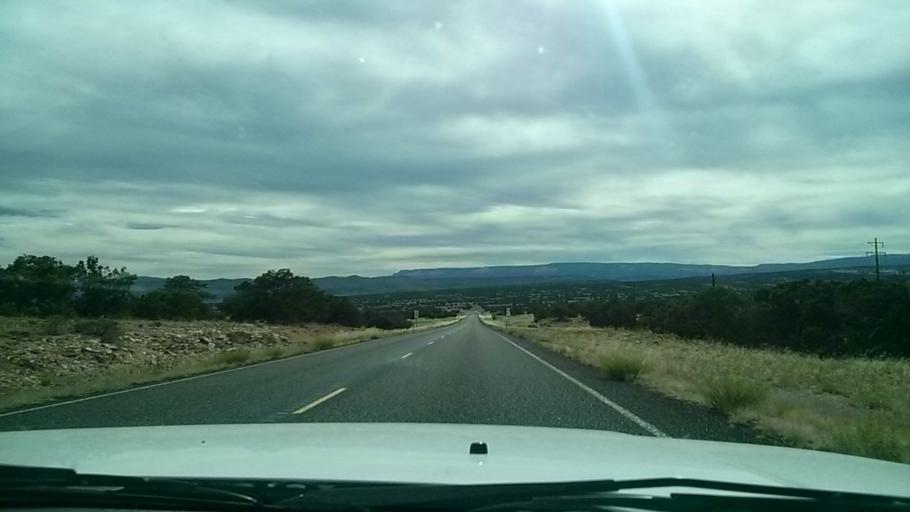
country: US
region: Utah
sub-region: Wayne County
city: Loa
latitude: 37.7500
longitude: -111.4757
